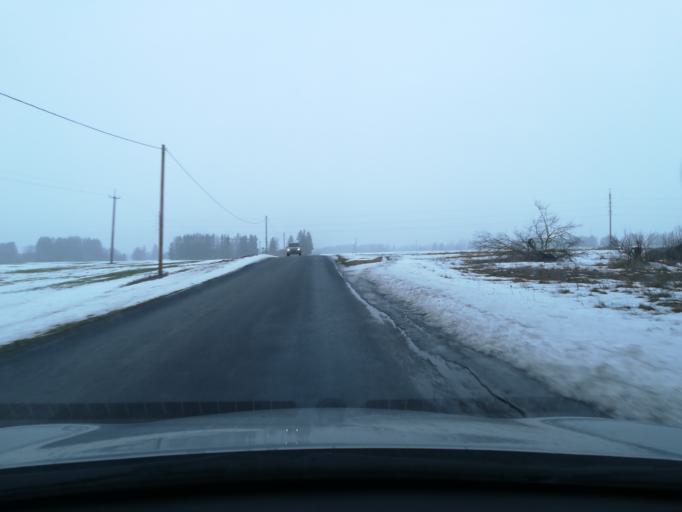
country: EE
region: Harju
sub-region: Raasiku vald
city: Raasiku
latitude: 59.3576
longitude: 25.2009
